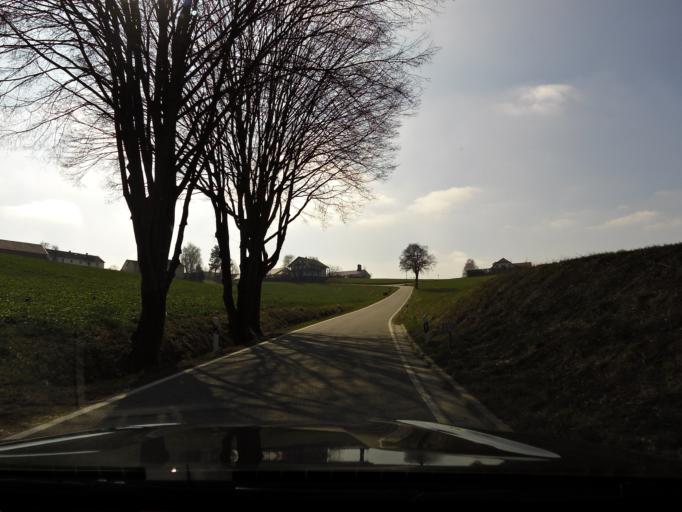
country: DE
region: Bavaria
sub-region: Lower Bavaria
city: Tiefenbach
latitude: 48.5089
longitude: 12.1114
